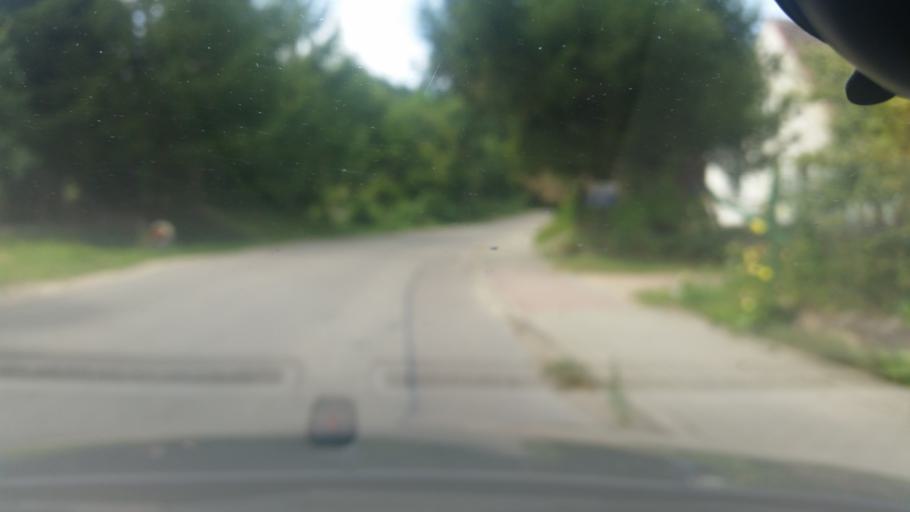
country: PL
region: Pomeranian Voivodeship
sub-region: Powiat wejherowski
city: Choczewo
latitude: 54.7564
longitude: 17.7847
